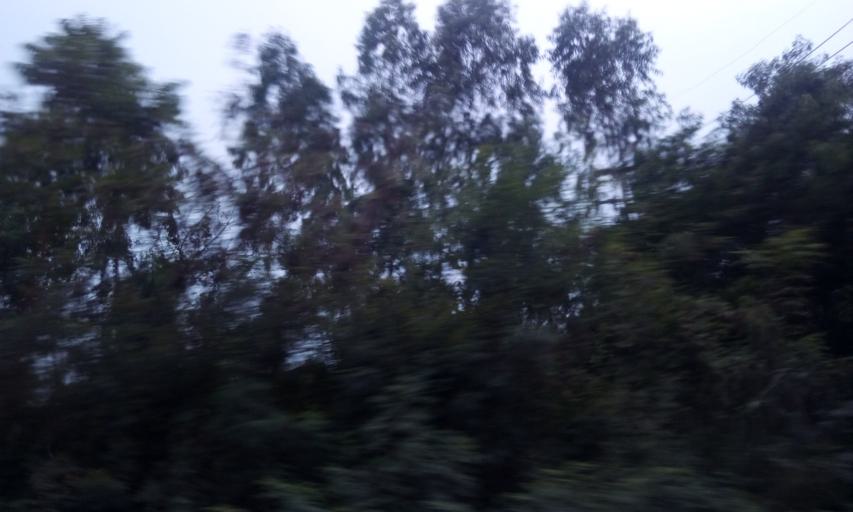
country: TH
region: Chachoengsao
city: Plaeng Yao
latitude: 13.5832
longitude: 101.2241
